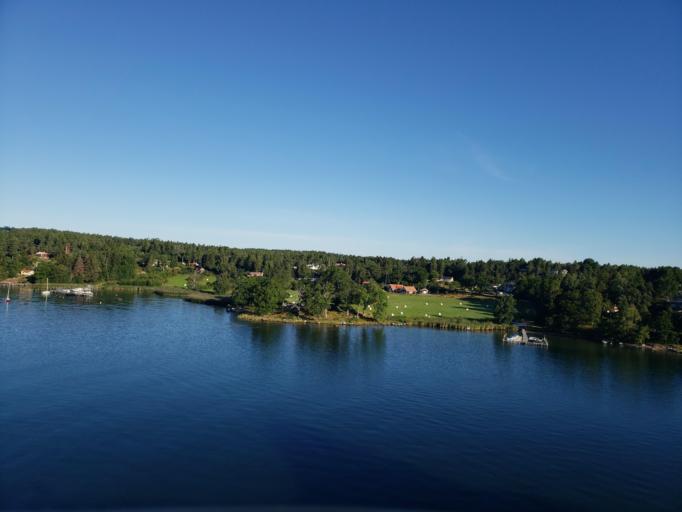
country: SE
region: Stockholm
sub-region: Vaxholms Kommun
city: Vaxholm
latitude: 59.5025
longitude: 18.4726
